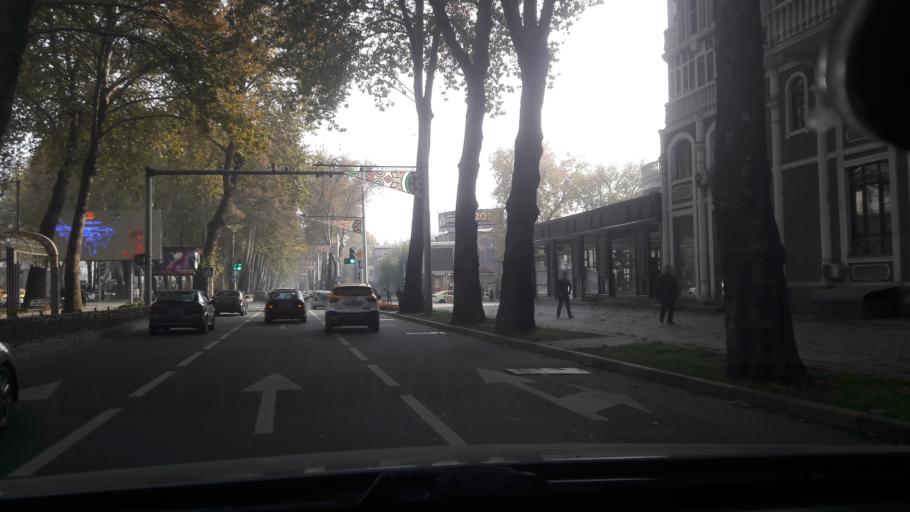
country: TJ
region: Dushanbe
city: Dushanbe
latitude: 38.5718
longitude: 68.7886
